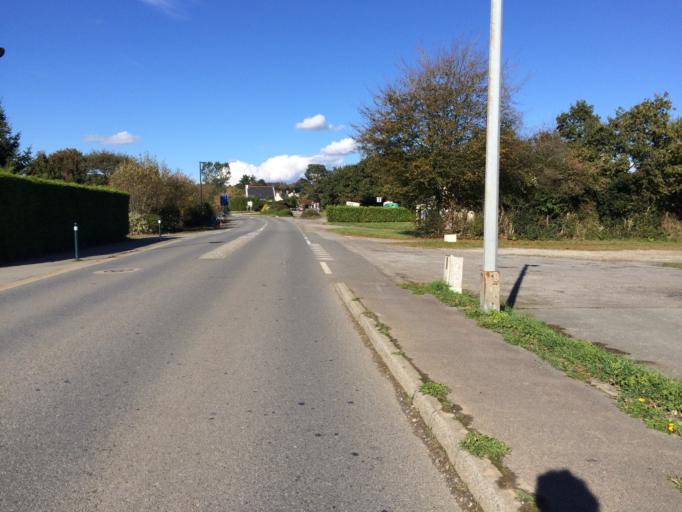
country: FR
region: Brittany
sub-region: Departement du Finistere
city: Saint-Urbain
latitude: 48.4027
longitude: -4.2281
